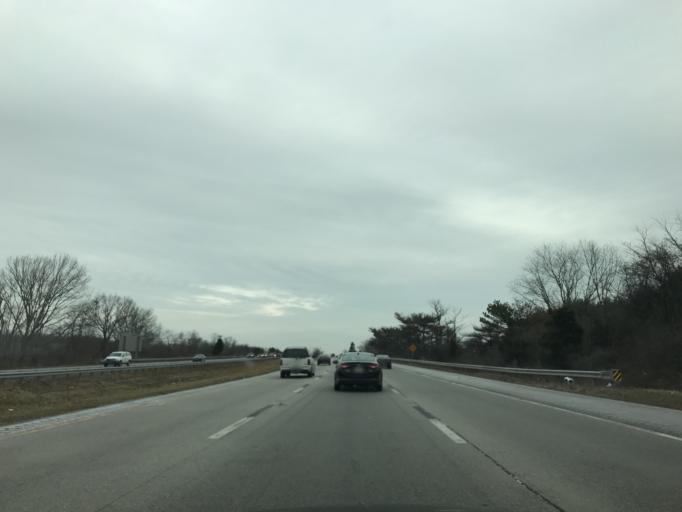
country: US
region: New Jersey
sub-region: Burlington County
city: Mount Laurel
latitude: 39.9724
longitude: -74.9038
